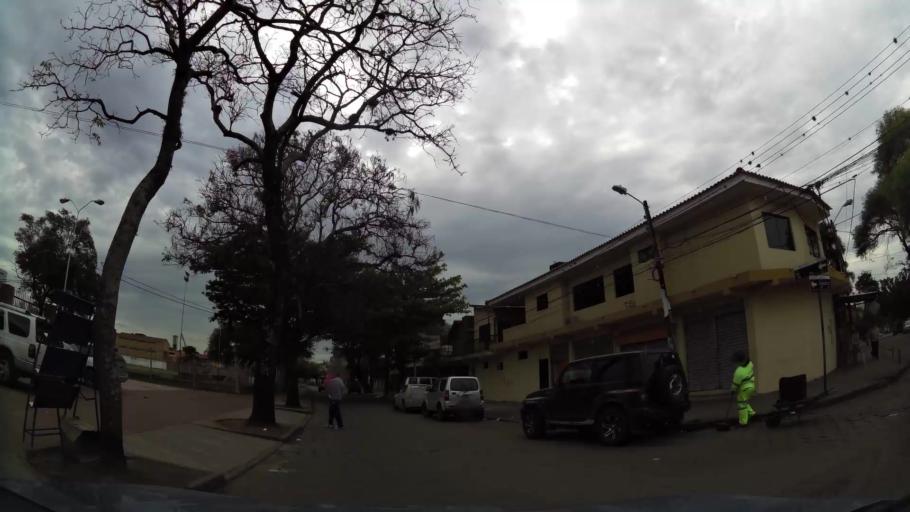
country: BO
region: Santa Cruz
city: Santa Cruz de la Sierra
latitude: -17.7752
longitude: -63.1719
